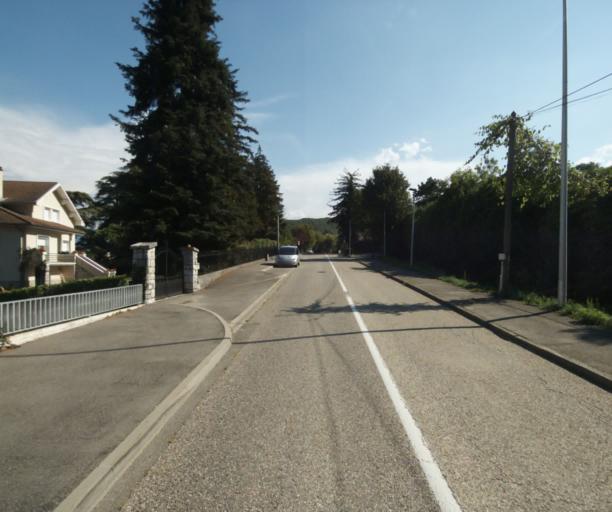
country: FR
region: Rhone-Alpes
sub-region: Departement de l'Isere
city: Seyssins
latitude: 45.1594
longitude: 5.6819
